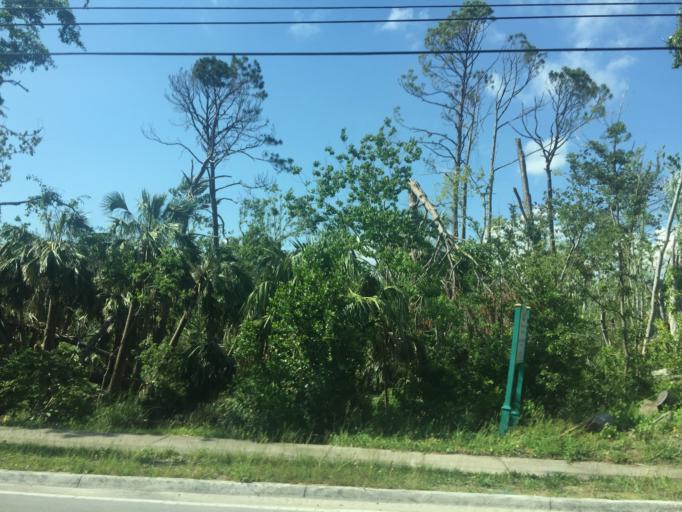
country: US
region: Florida
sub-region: Bay County
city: Panama City
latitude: 30.1677
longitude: -85.6451
